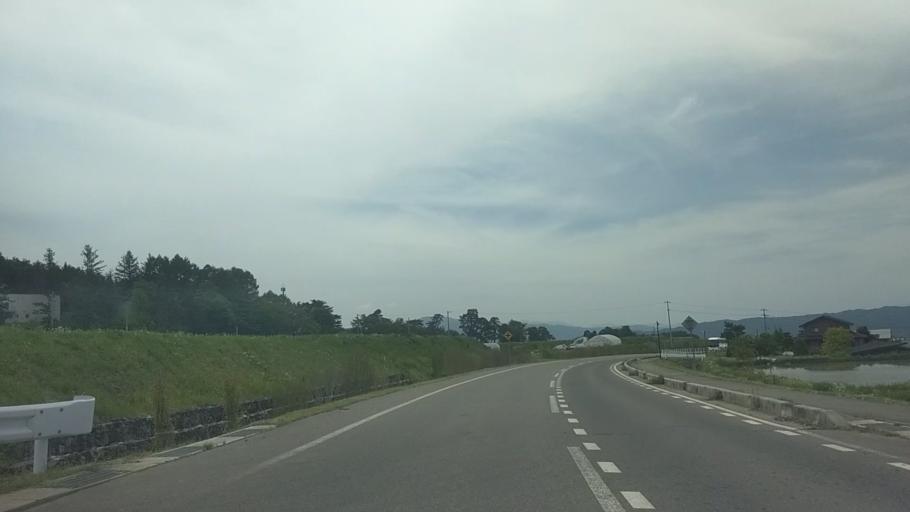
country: JP
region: Nagano
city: Chino
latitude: 36.0253
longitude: 138.2322
